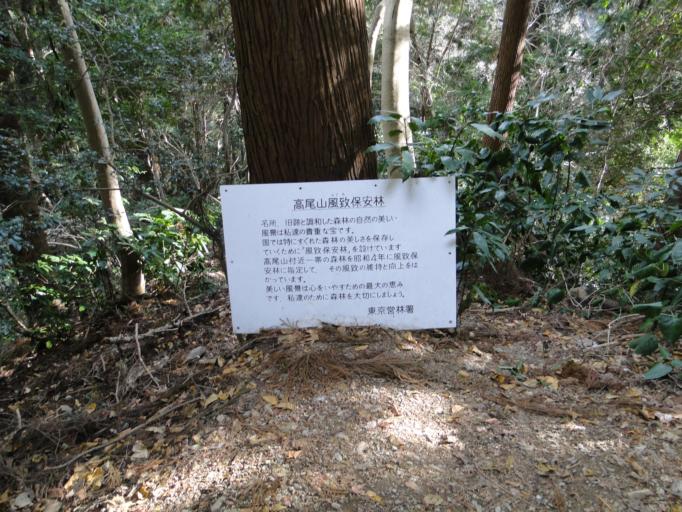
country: JP
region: Tokyo
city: Hachioji
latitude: 35.6283
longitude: 139.2526
